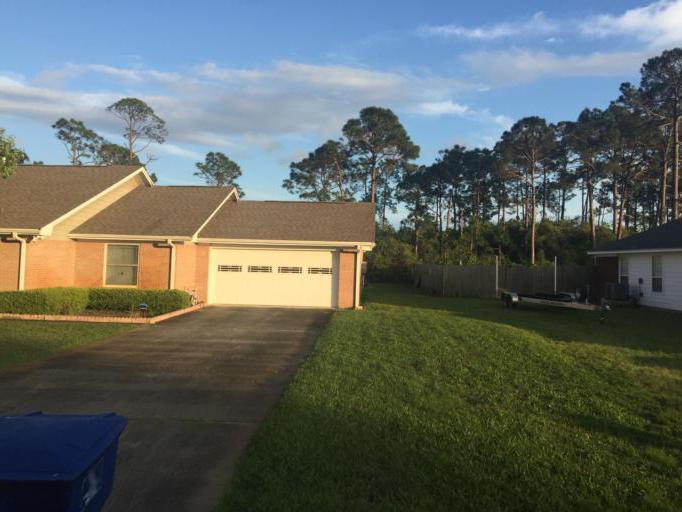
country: US
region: Florida
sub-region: Bay County
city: Panama City Beach
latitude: 30.2255
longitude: -85.8431
